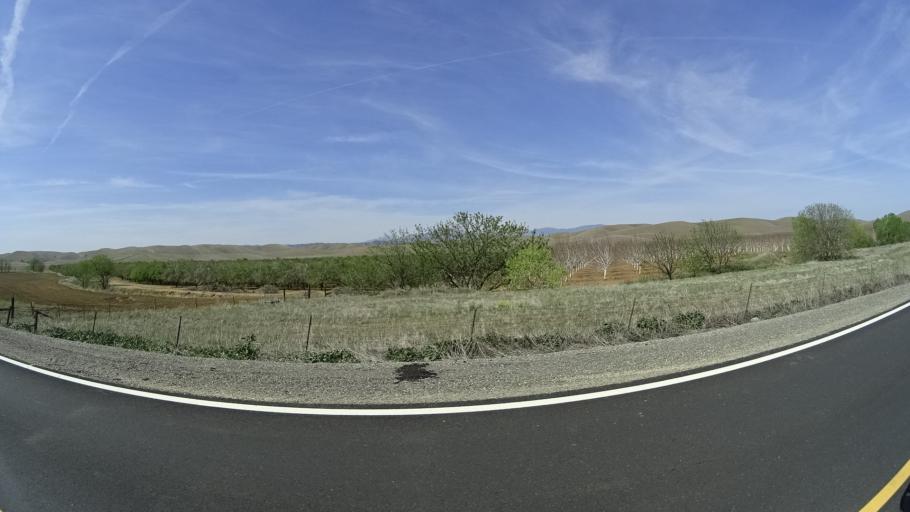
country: US
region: California
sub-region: Glenn County
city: Willows
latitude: 39.5345
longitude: -122.3428
